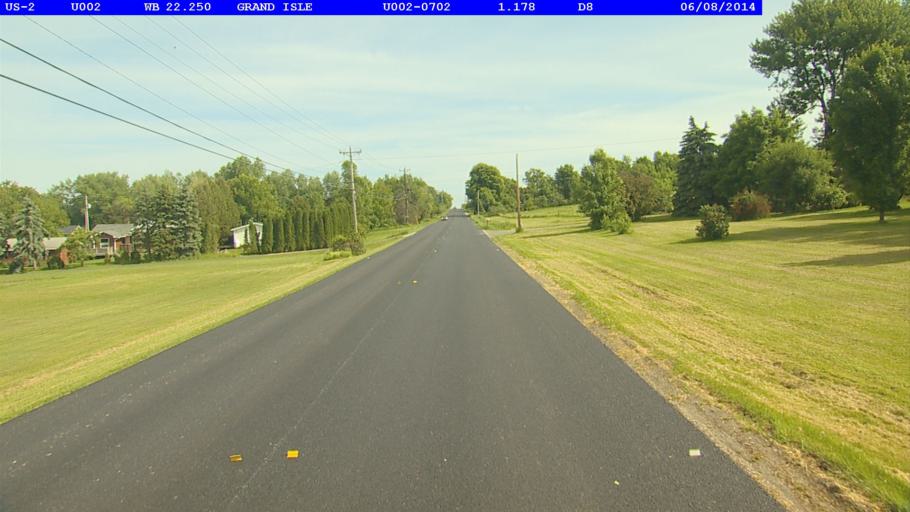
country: US
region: Vermont
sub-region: Grand Isle County
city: North Hero
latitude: 44.7504
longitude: -73.2876
